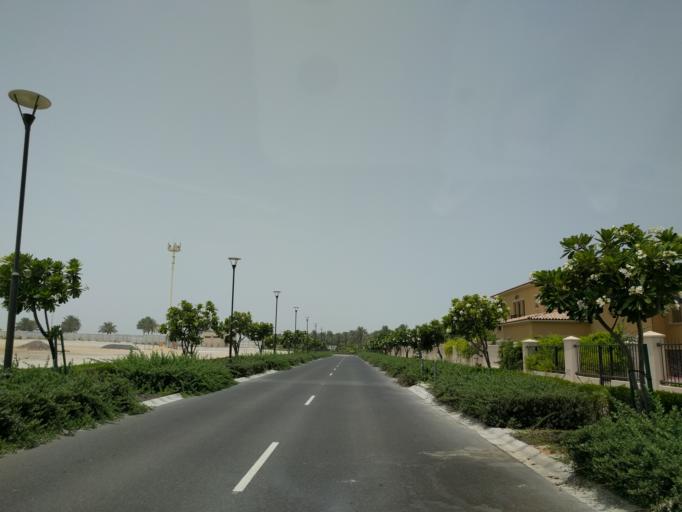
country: AE
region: Abu Dhabi
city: Abu Dhabi
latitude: 24.5439
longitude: 54.4434
